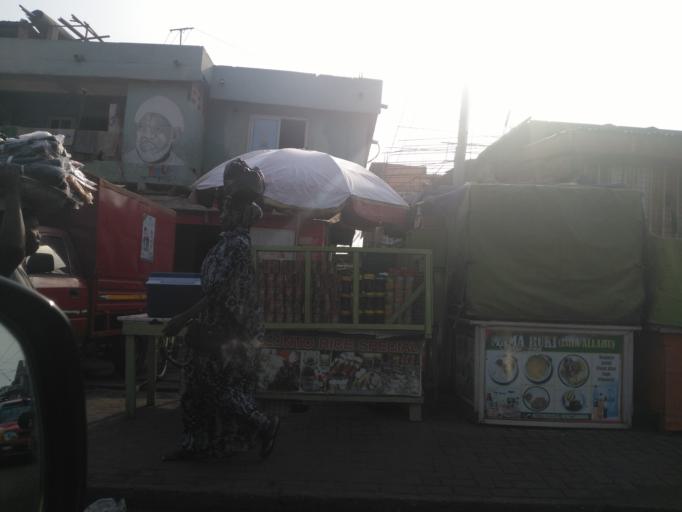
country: GH
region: Greater Accra
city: Accra
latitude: 5.5875
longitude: -0.1968
